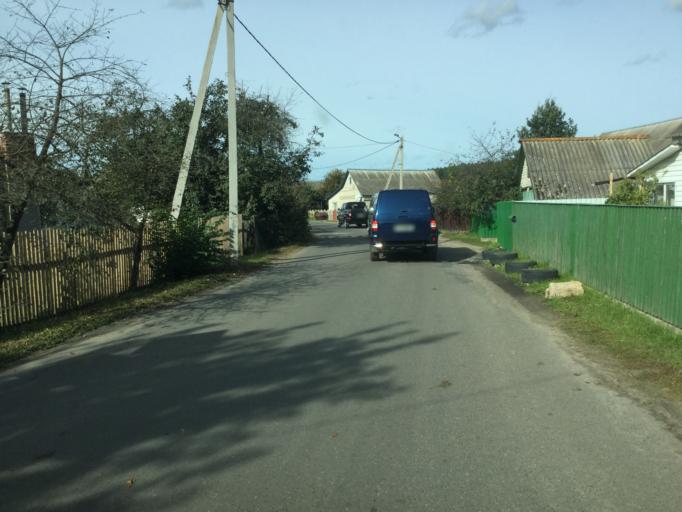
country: BY
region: Vitebsk
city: Orsha
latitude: 54.5475
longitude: 30.4335
